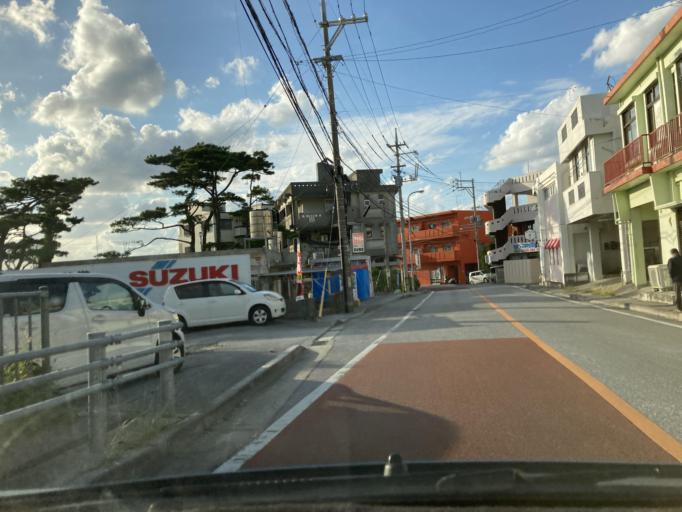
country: JP
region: Okinawa
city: Chatan
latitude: 26.3186
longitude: 127.7774
